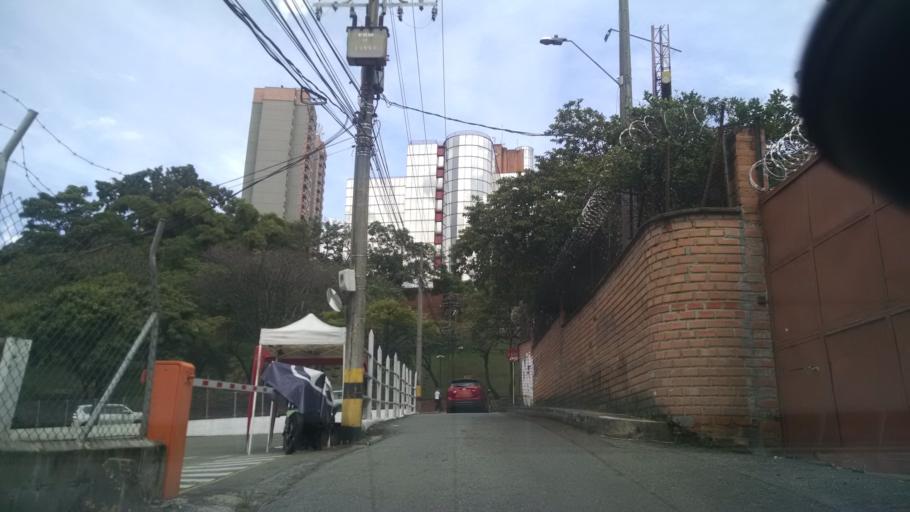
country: CO
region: Antioquia
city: Medellin
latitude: 6.2171
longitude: -75.5704
